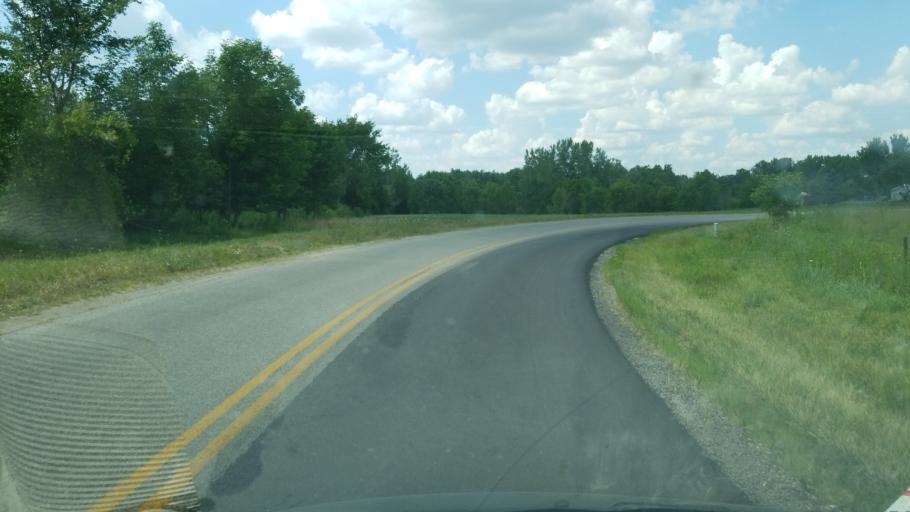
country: US
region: Ohio
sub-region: Champaign County
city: North Lewisburg
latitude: 40.3424
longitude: -83.4874
